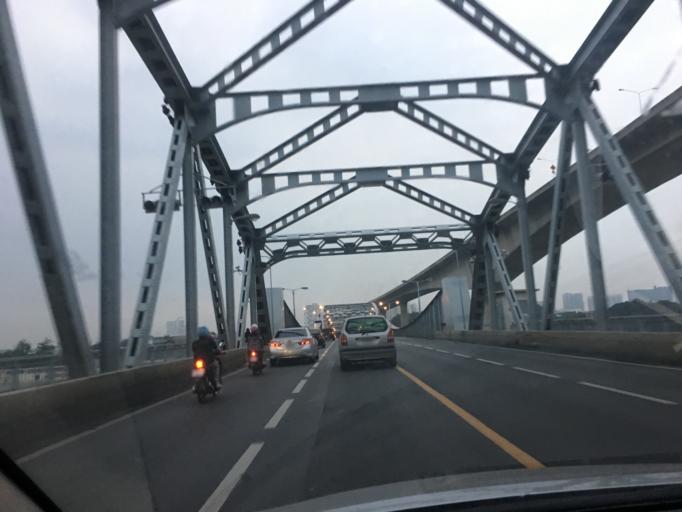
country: TH
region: Bangkok
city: Bang Kho Laem
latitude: 13.7004
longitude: 100.4928
